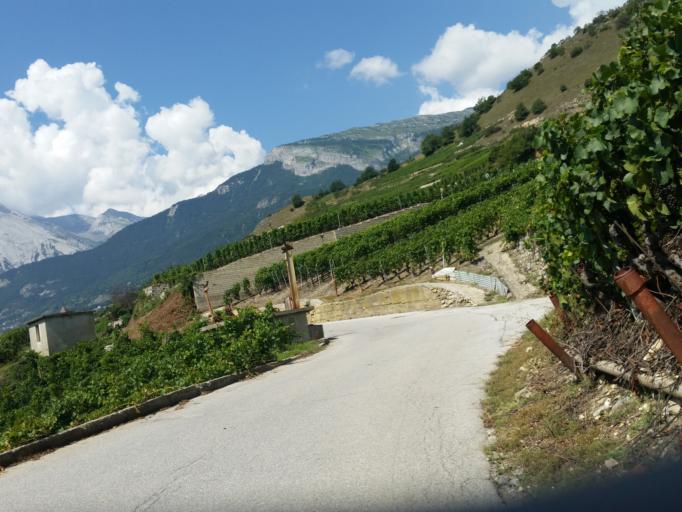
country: CH
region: Valais
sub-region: Conthey District
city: Conthey
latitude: 46.2366
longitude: 7.3249
